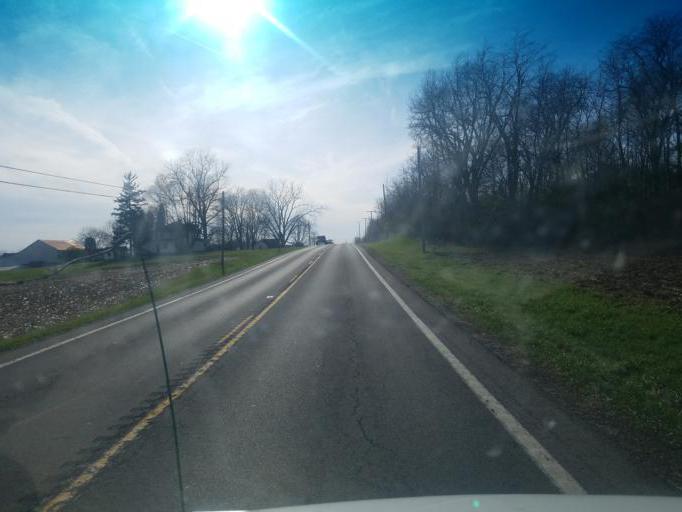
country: US
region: Ohio
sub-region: Logan County
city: Bellefontaine
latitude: 40.3638
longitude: -83.8014
